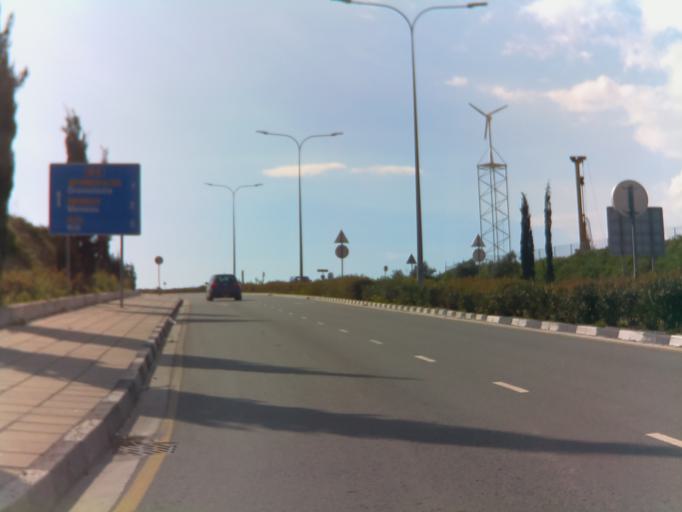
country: CY
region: Larnaka
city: Dhromolaxia
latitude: 34.8752
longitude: 33.6020
